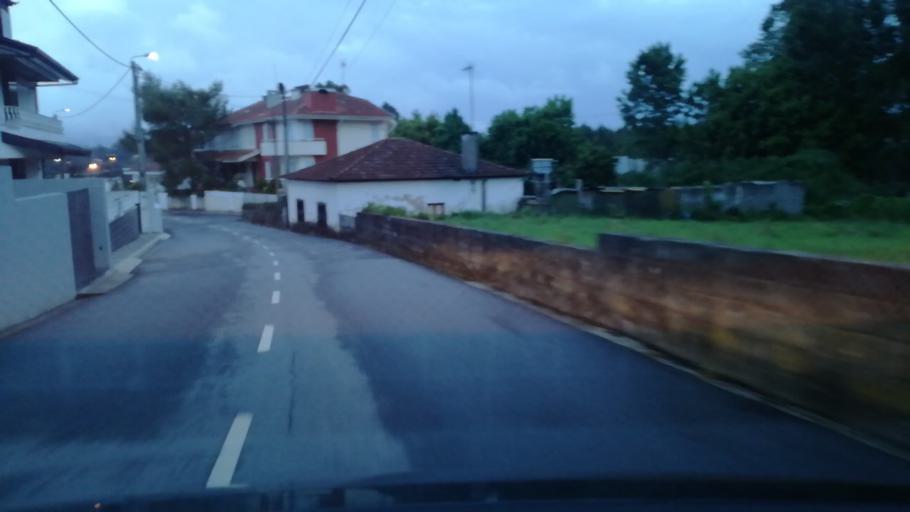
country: PT
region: Porto
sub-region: Maia
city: Anta
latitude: 41.2519
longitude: -8.6269
